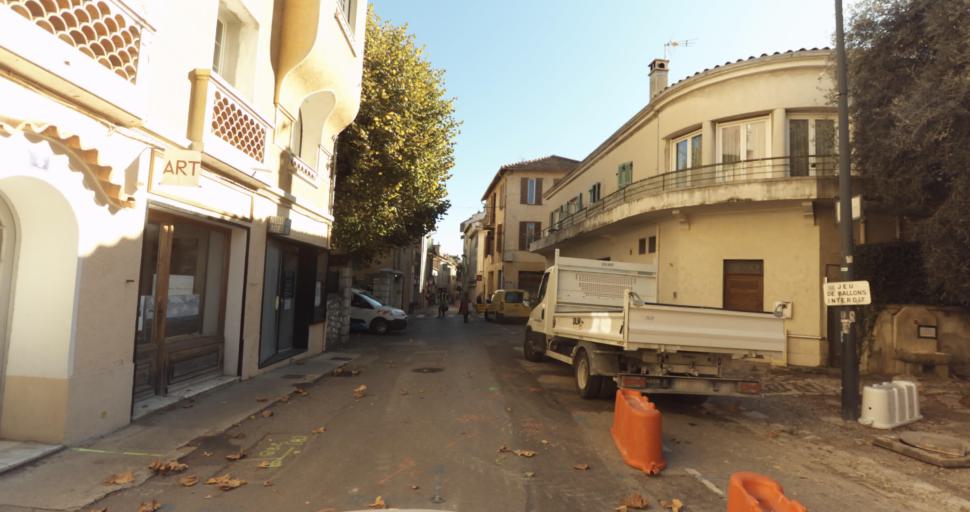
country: FR
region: Provence-Alpes-Cote d'Azur
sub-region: Departement des Alpes-Maritimes
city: Vence
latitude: 43.7233
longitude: 7.1098
